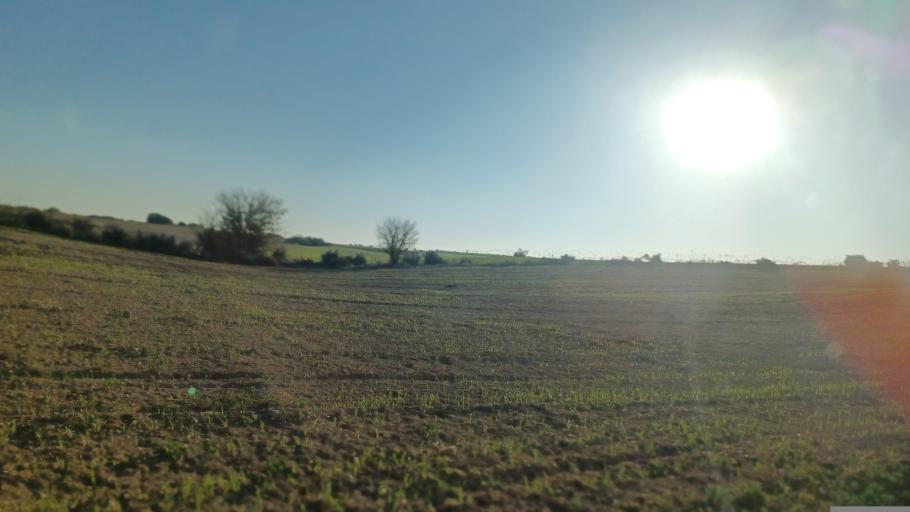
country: CY
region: Lefkosia
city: Kato Deftera
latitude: 35.1482
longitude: 33.2679
